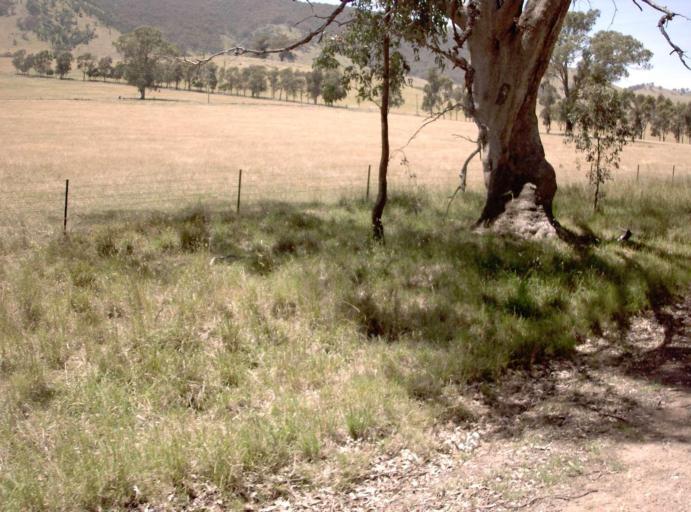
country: AU
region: Victoria
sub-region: East Gippsland
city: Bairnsdale
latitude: -37.3276
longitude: 147.7781
